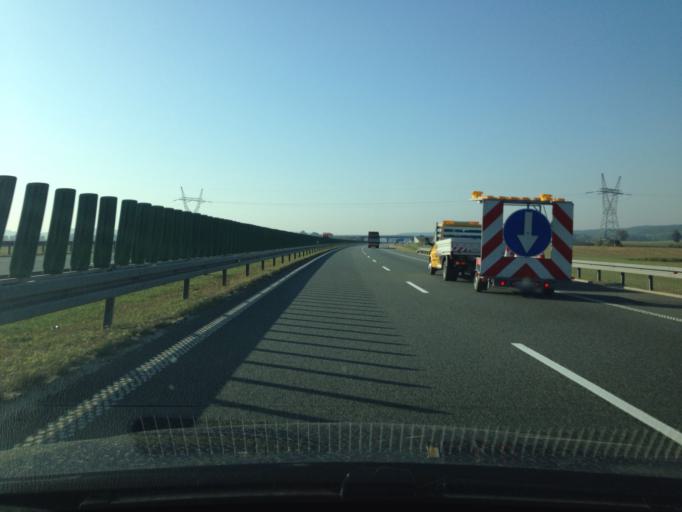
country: PL
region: Pomeranian Voivodeship
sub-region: Powiat tczewski
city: Pelplin
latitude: 53.9644
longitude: 18.6574
